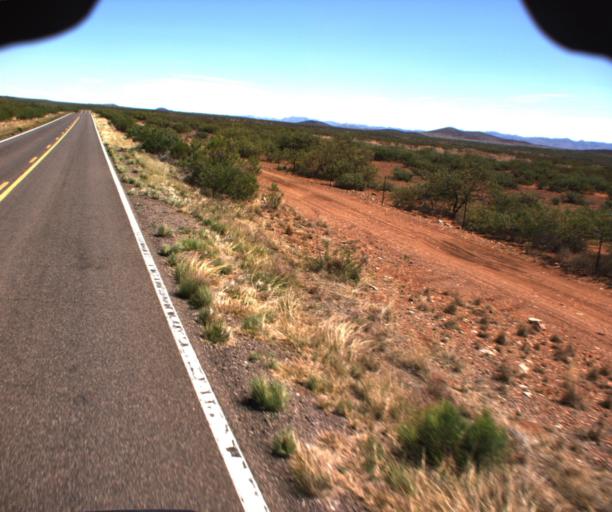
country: US
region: Arizona
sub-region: Cochise County
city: Douglas
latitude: 31.4866
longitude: -109.3439
